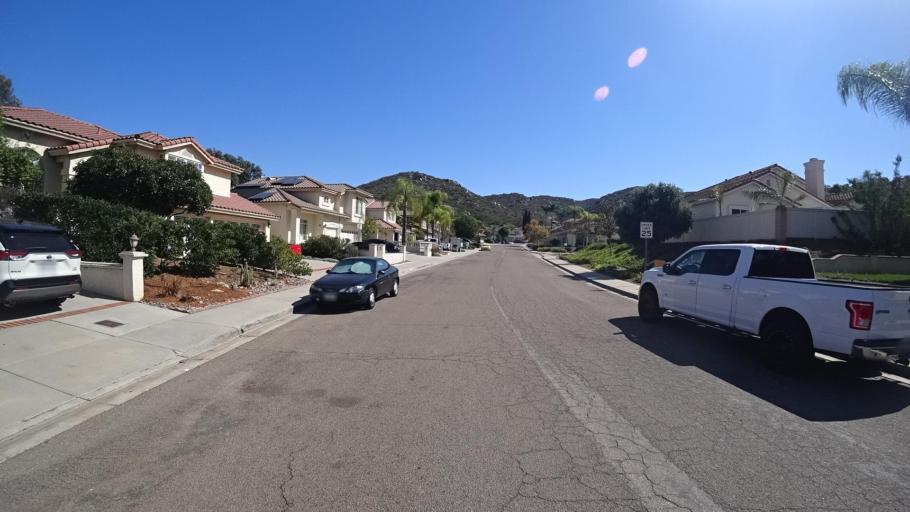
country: US
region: California
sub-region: San Diego County
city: Rancho San Diego
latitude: 32.7368
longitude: -116.9127
